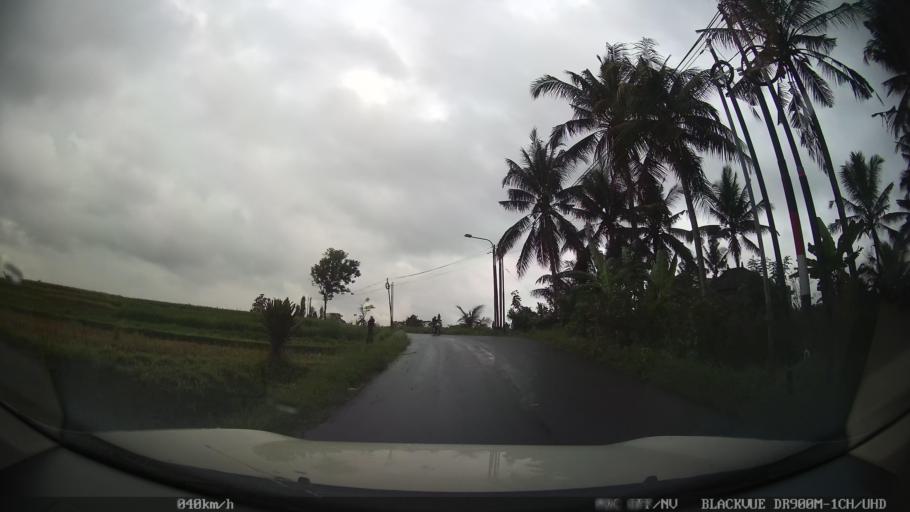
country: ID
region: Bali
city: Banjar Teguan
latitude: -8.5041
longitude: 115.2267
